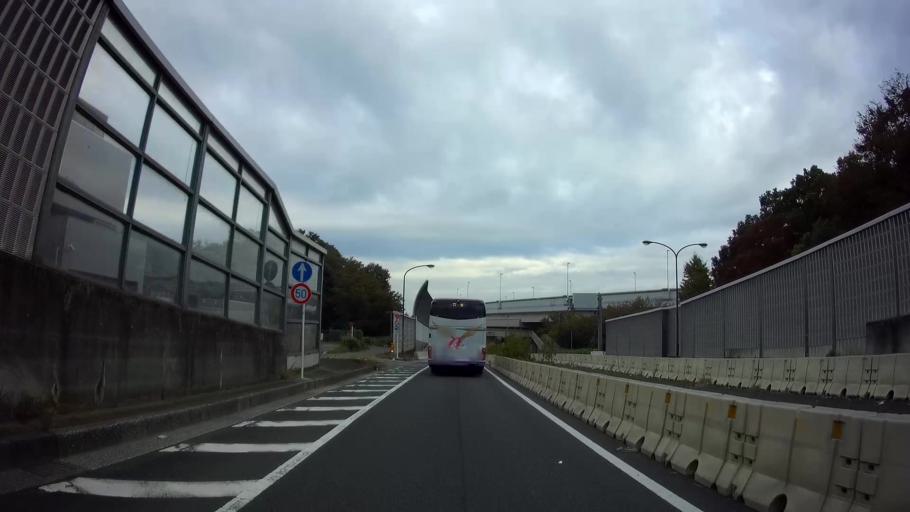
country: JP
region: Saitama
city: Wako
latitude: 35.7848
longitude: 139.6459
